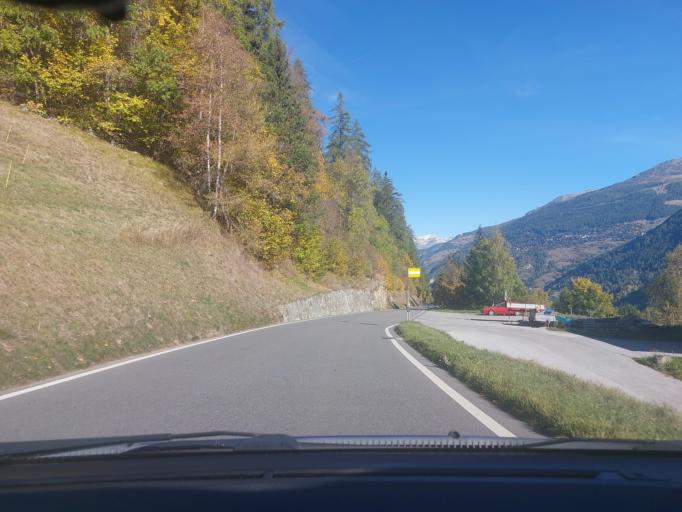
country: CH
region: Valais
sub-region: Sierre District
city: Chippis
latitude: 46.1856
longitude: 7.5846
